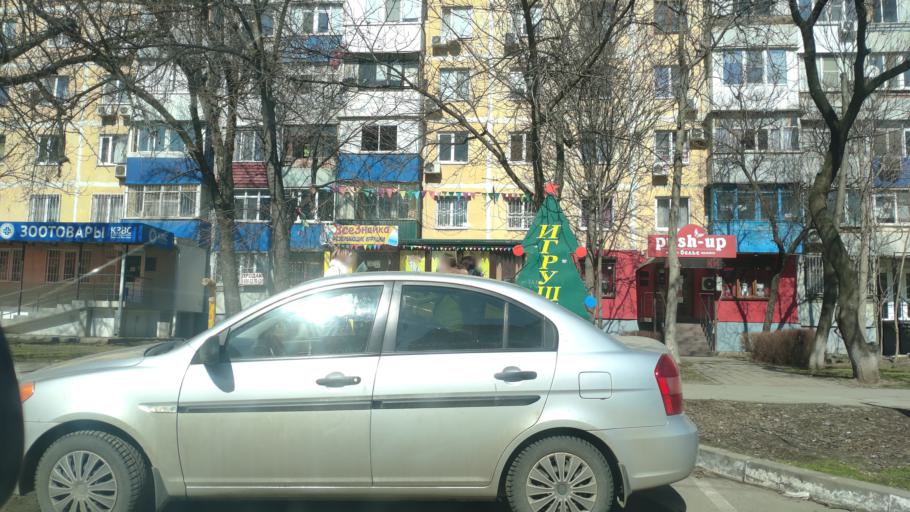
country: RU
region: Krasnodarskiy
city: Krasnodar
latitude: 45.0557
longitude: 39.0194
